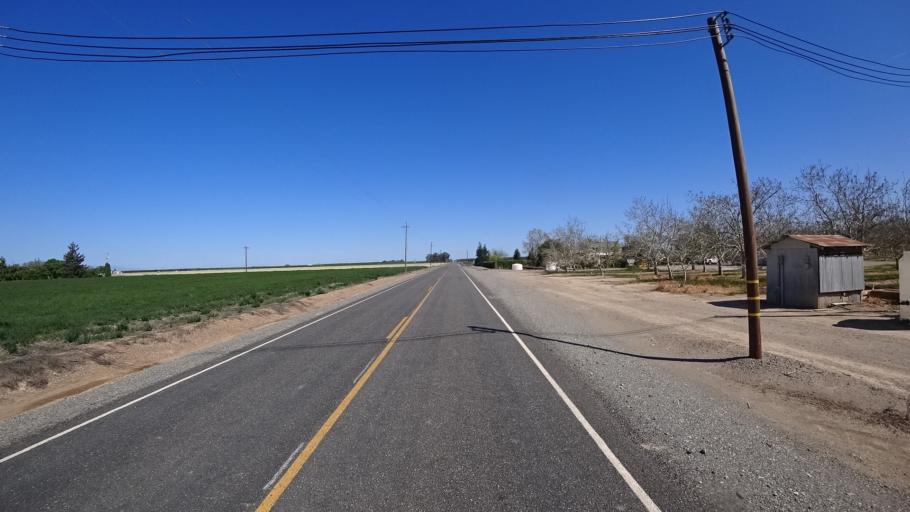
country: US
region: California
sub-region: Glenn County
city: Hamilton City
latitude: 39.6510
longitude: -122.1037
